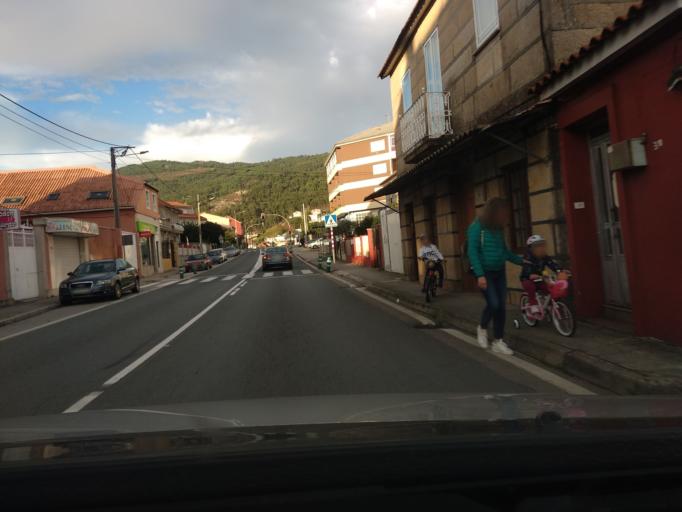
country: ES
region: Galicia
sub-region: Provincia de Pontevedra
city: Moana
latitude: 42.2868
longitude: -8.7220
